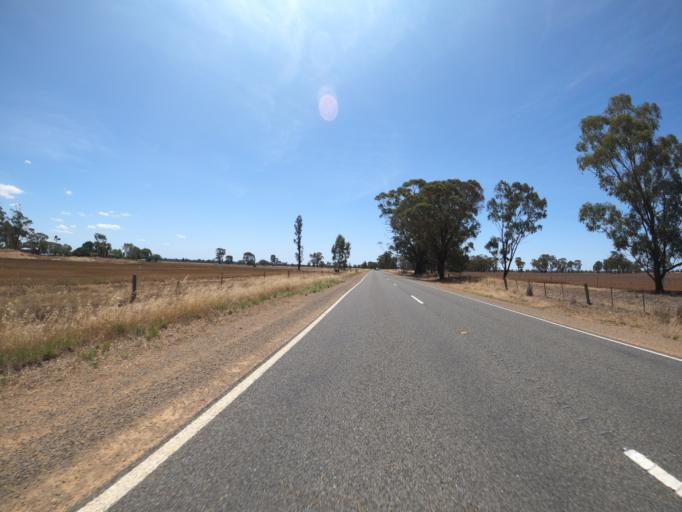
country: AU
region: Victoria
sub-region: Moira
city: Yarrawonga
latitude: -36.2023
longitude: 145.9672
